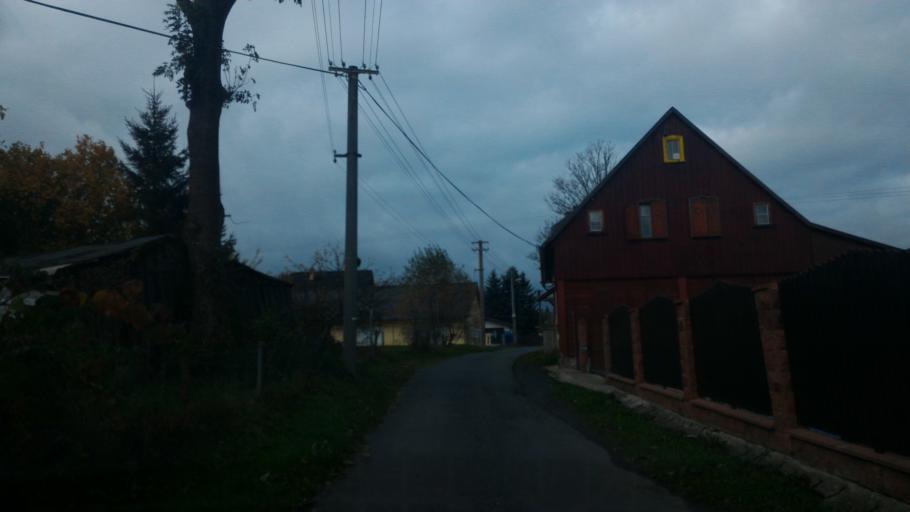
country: CZ
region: Ustecky
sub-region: Okres Decin
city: Krasna Lipa
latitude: 50.8819
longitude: 14.5462
